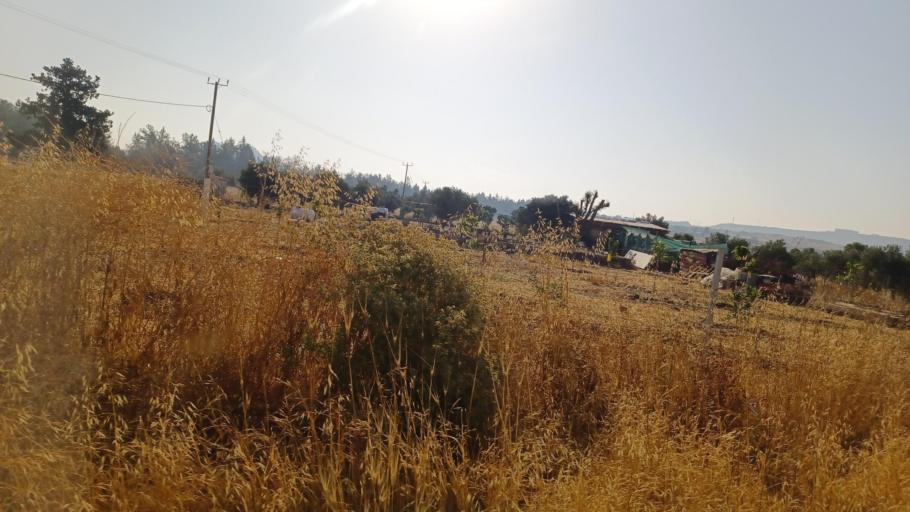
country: CY
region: Lefkosia
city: Lympia
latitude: 34.9948
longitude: 33.4369
